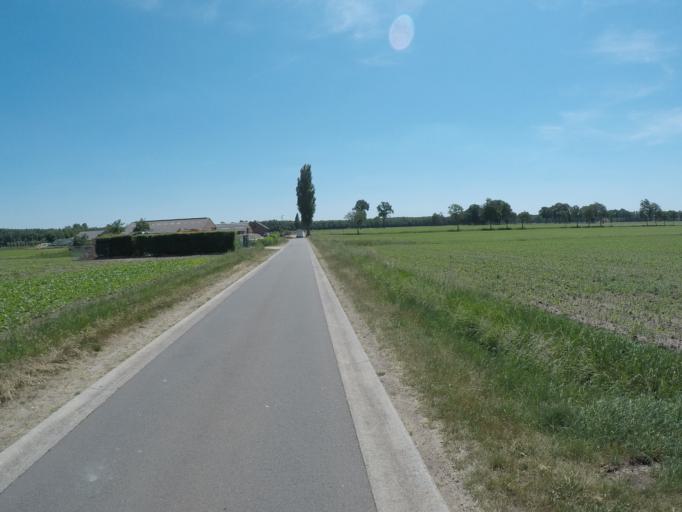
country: BE
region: Flanders
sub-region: Provincie Antwerpen
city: Wuustwezel
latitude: 51.3750
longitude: 4.5632
